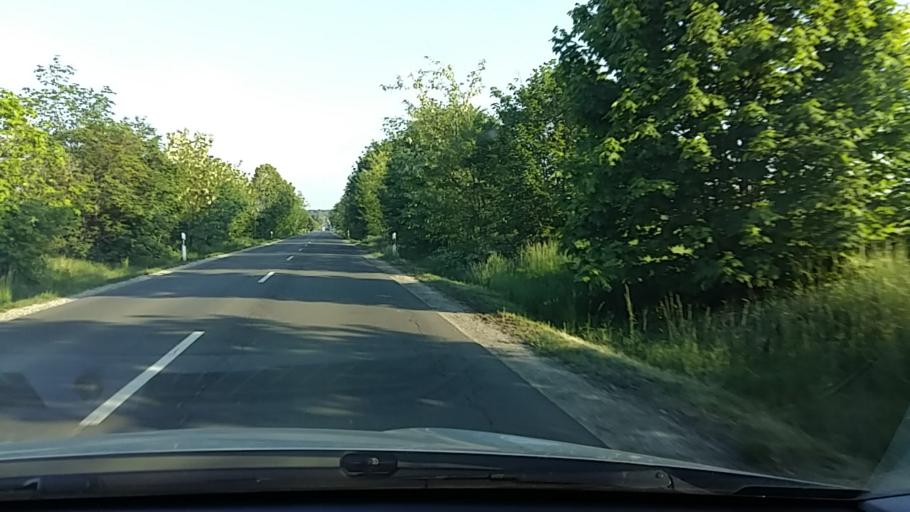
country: HU
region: Pest
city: Szod
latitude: 47.7252
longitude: 19.2273
